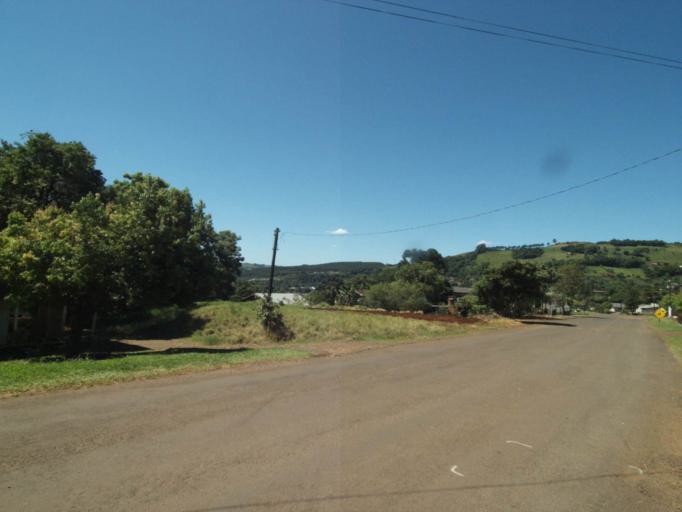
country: BR
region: Parana
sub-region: Ampere
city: Ampere
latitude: -26.1792
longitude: -53.3622
